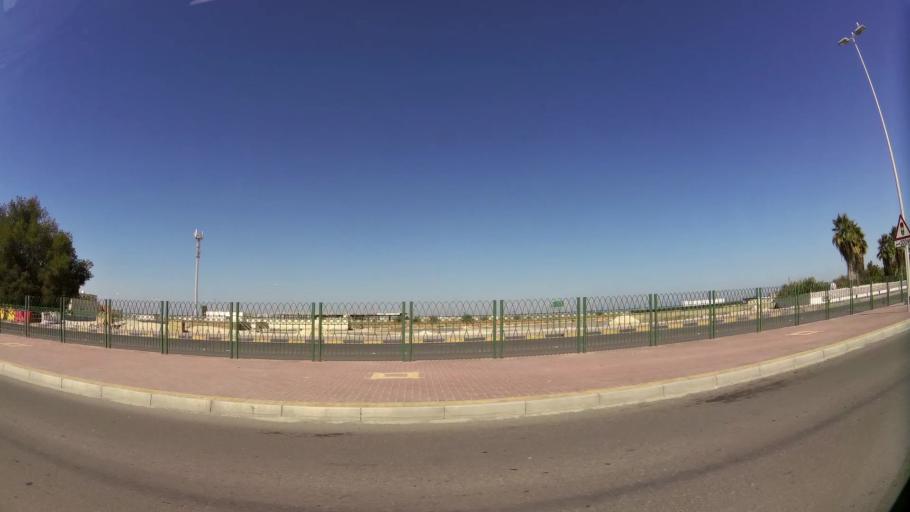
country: BH
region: Muharraq
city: Al Hadd
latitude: 26.2550
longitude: 50.6492
